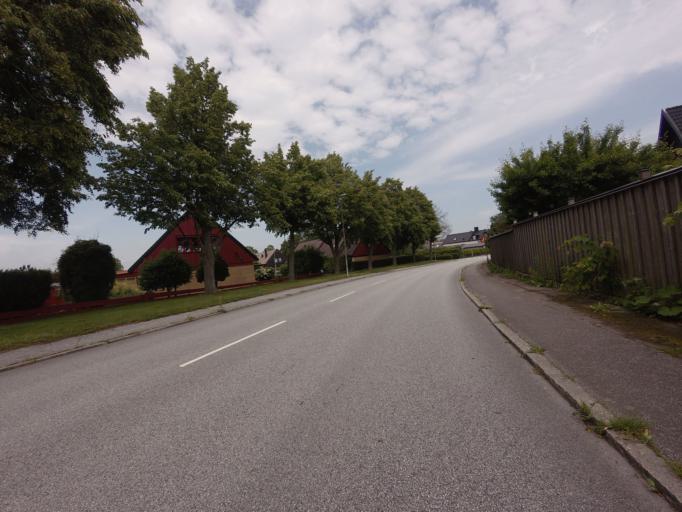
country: SE
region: Skane
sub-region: Ystads Kommun
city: Ystad
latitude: 55.4284
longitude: 13.7989
